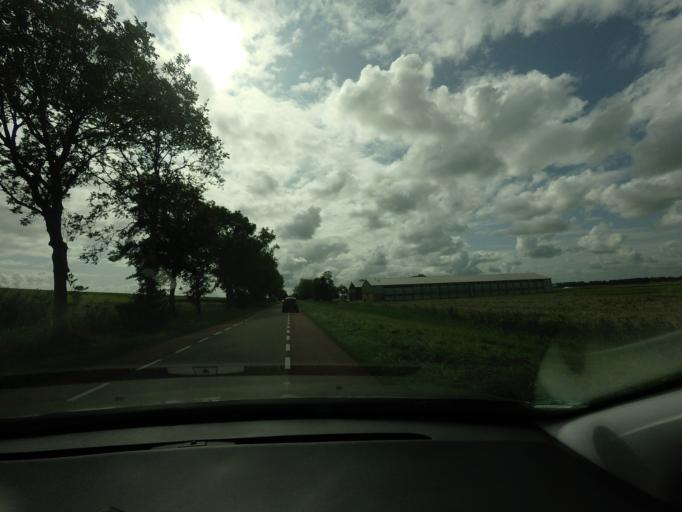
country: NL
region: North Holland
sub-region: Gemeente Medemblik
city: Medemblik
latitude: 52.8042
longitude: 5.1064
